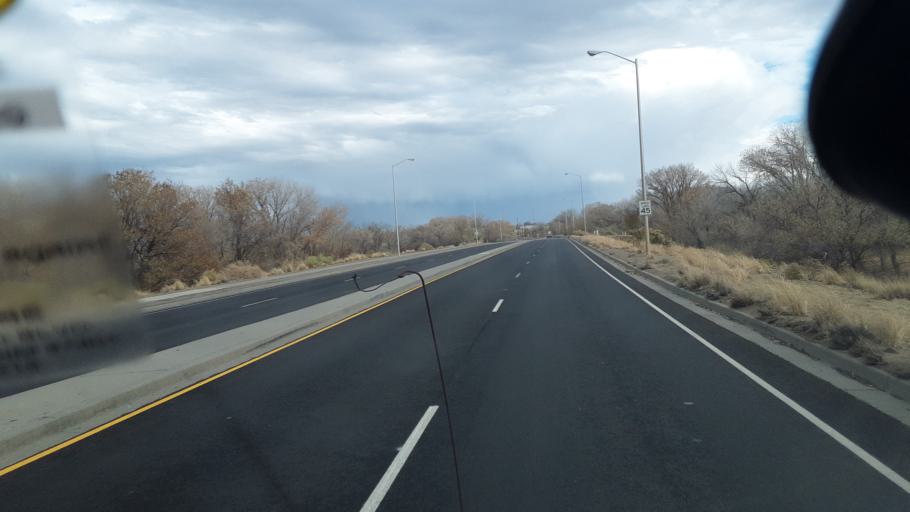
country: US
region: New Mexico
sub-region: San Juan County
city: Farmington
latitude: 36.7191
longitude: -108.2112
